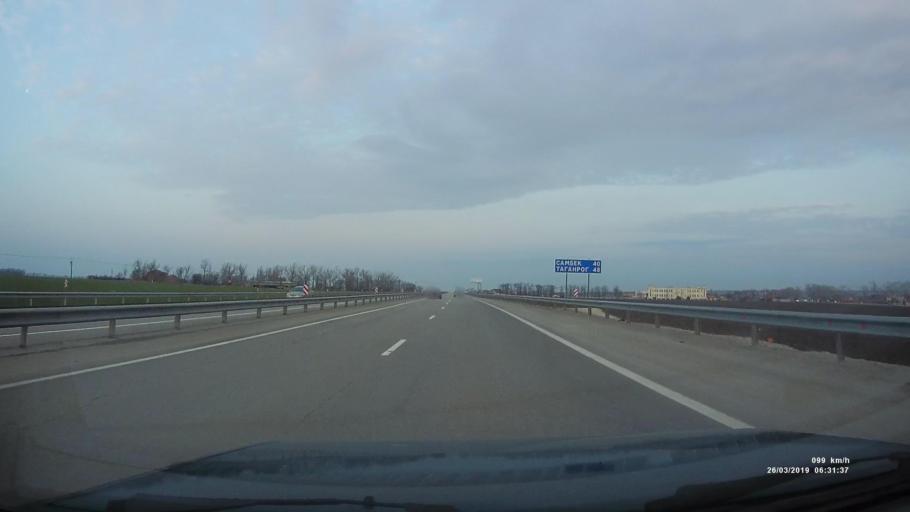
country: RU
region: Rostov
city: Krym
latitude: 47.2729
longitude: 39.5288
